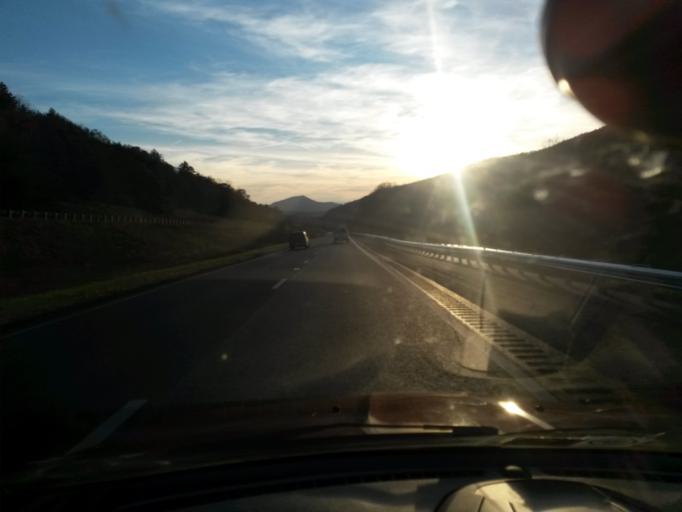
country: US
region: Virginia
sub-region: Alleghany County
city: Clifton Forge
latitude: 37.8378
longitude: -79.6456
